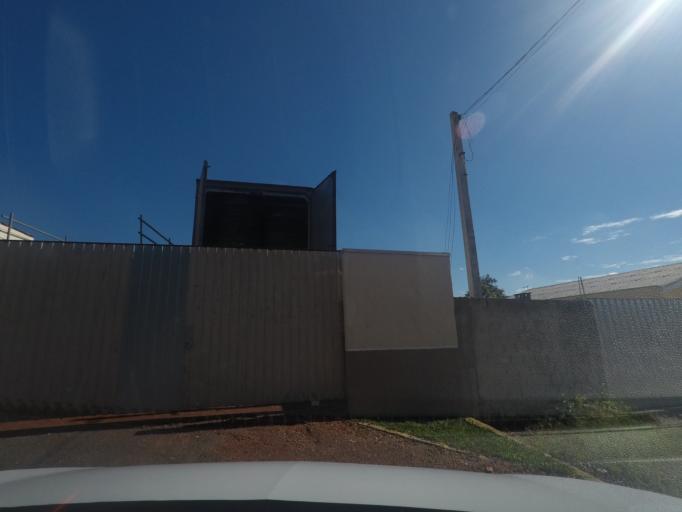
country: BR
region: Parana
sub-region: Sao Jose Dos Pinhais
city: Sao Jose dos Pinhais
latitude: -25.5087
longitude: -49.2772
